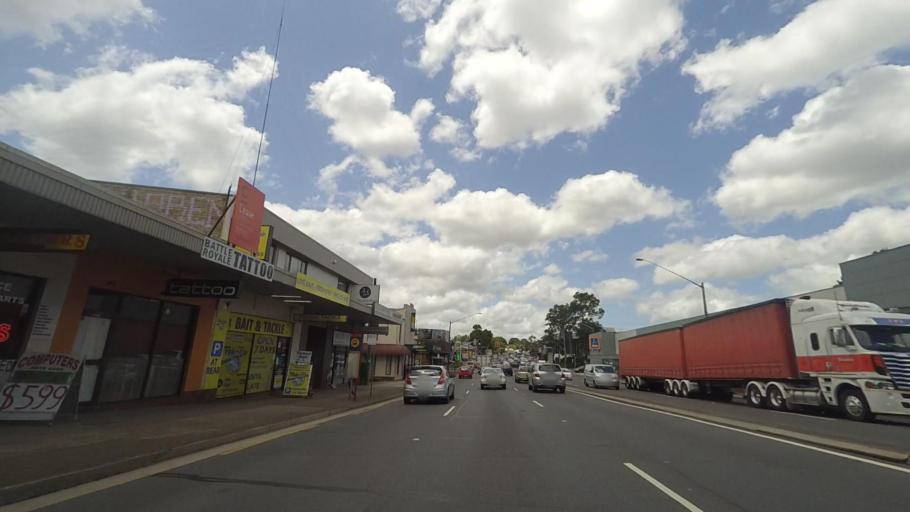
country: AU
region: New South Wales
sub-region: Hornsby Shire
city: Pennant Hills
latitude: -33.7320
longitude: 151.0792
